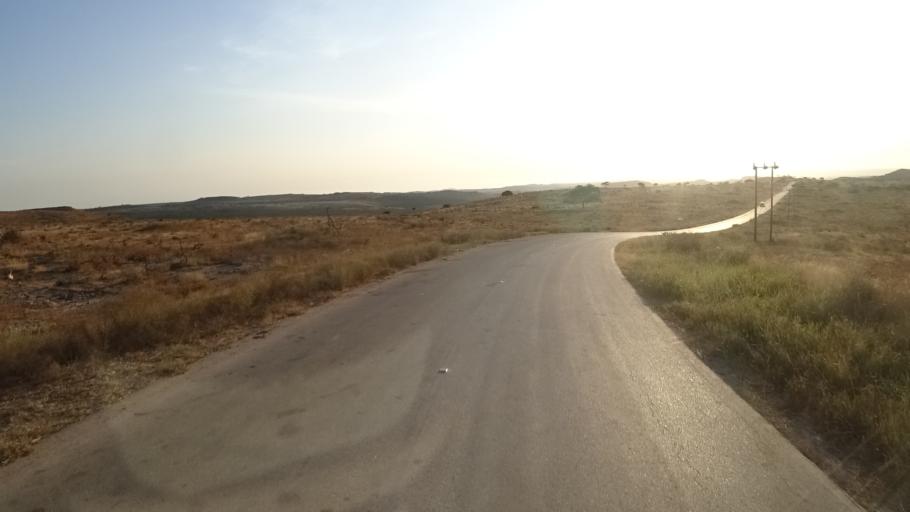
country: OM
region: Zufar
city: Salalah
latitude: 17.1477
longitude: 54.6172
